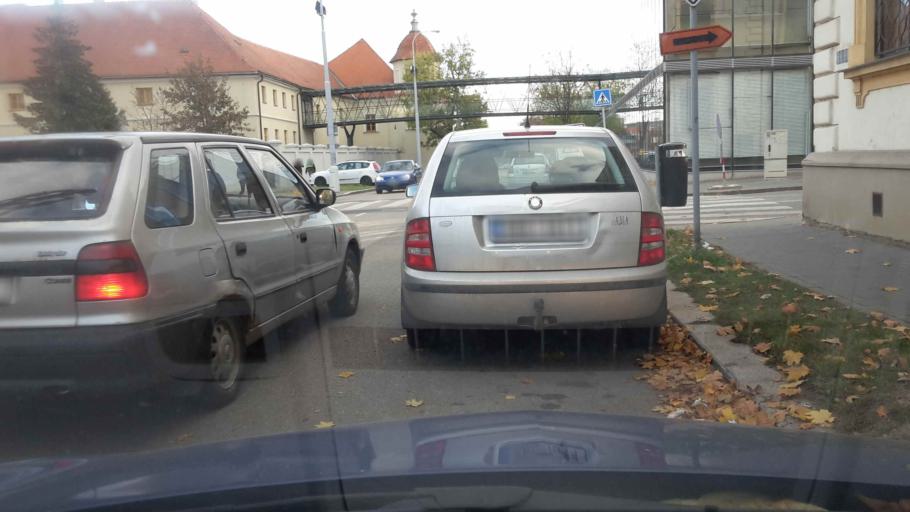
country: CZ
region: South Moravian
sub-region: Mesto Brno
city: Brno
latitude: 49.2273
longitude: 16.5955
